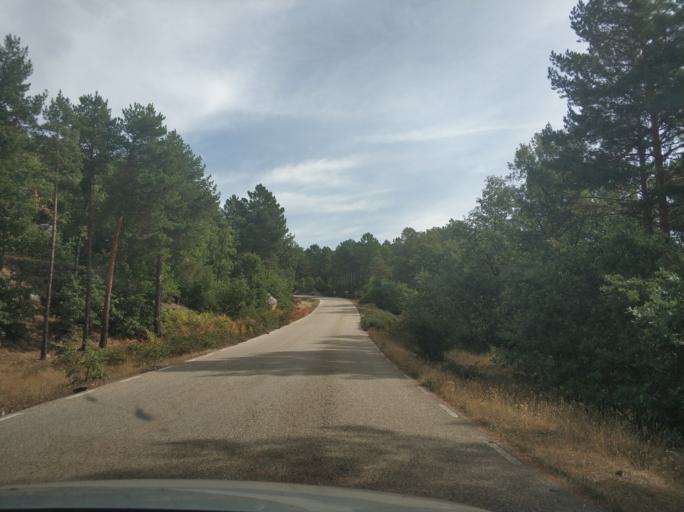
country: ES
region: Castille and Leon
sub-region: Provincia de Soria
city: Duruelo de la Sierra
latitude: 41.8950
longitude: -2.9454
